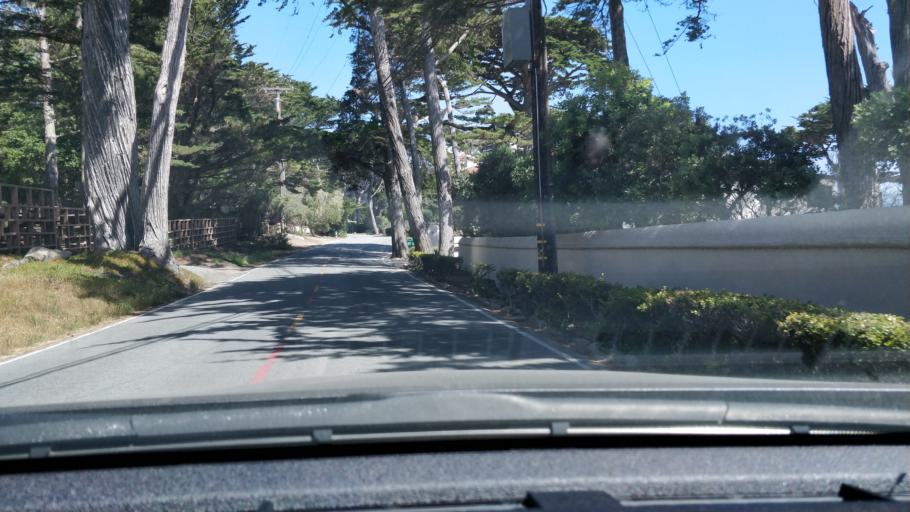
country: US
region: California
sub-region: Monterey County
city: Del Monte Forest
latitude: 36.5667
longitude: -121.9595
